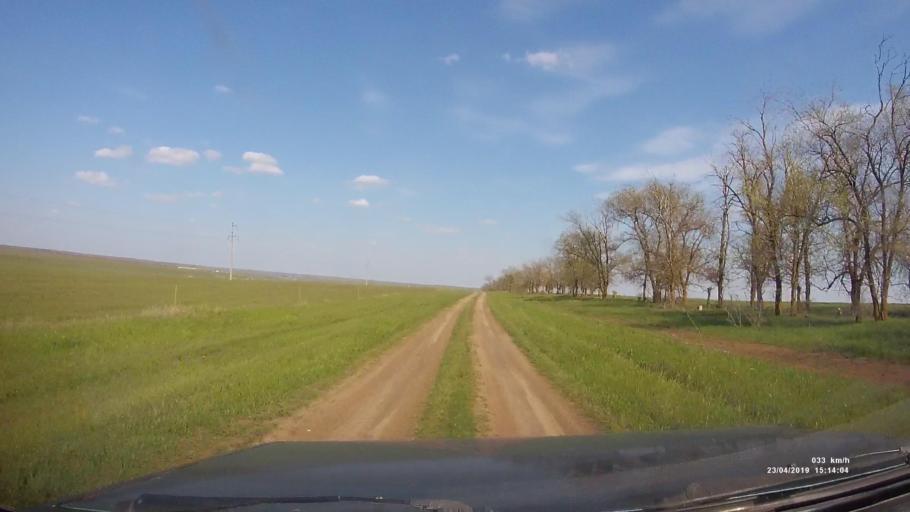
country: RU
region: Rostov
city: Remontnoye
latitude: 46.5397
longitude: 42.9604
